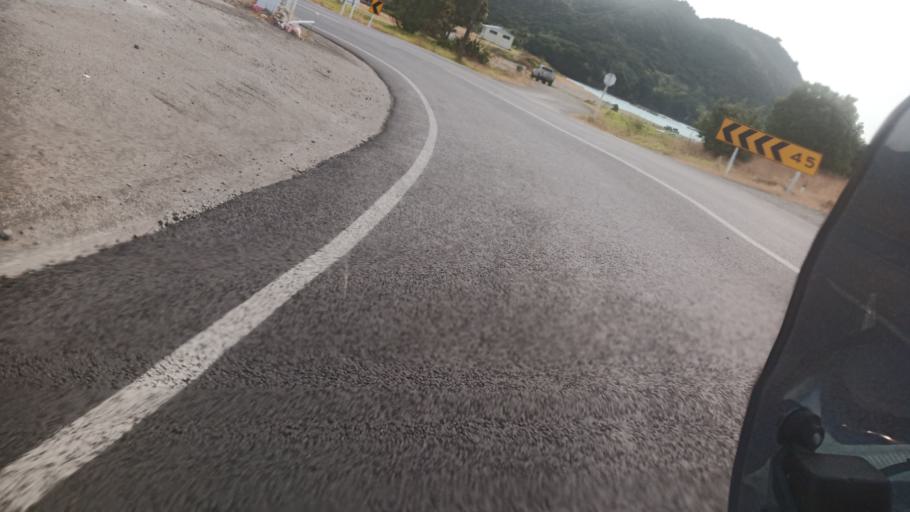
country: NZ
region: Bay of Plenty
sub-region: Opotiki District
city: Opotiki
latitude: -37.8136
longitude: 177.6332
